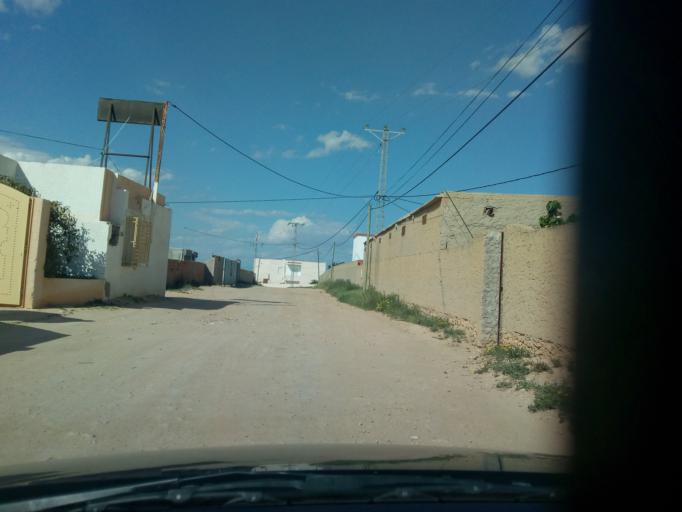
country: TN
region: Safaqis
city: Sfax
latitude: 34.7286
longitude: 10.6050
